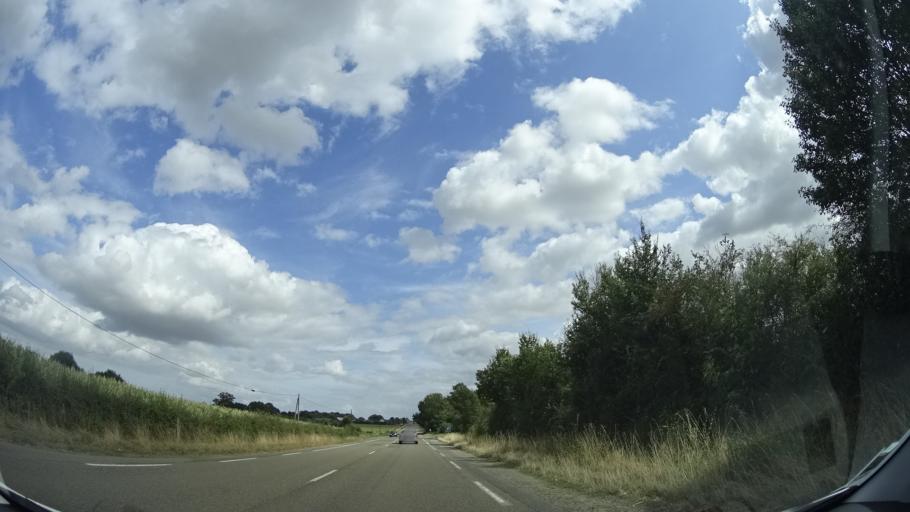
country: FR
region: Pays de la Loire
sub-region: Departement de la Mayenne
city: Soulge-sur-Ouette
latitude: 48.0618
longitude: -0.5915
